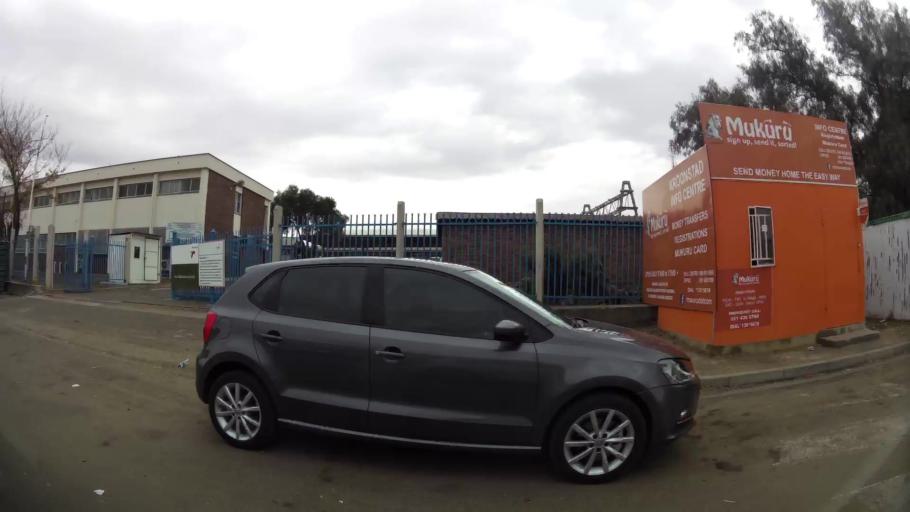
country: ZA
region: Orange Free State
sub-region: Fezile Dabi District Municipality
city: Kroonstad
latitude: -27.6603
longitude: 27.2343
